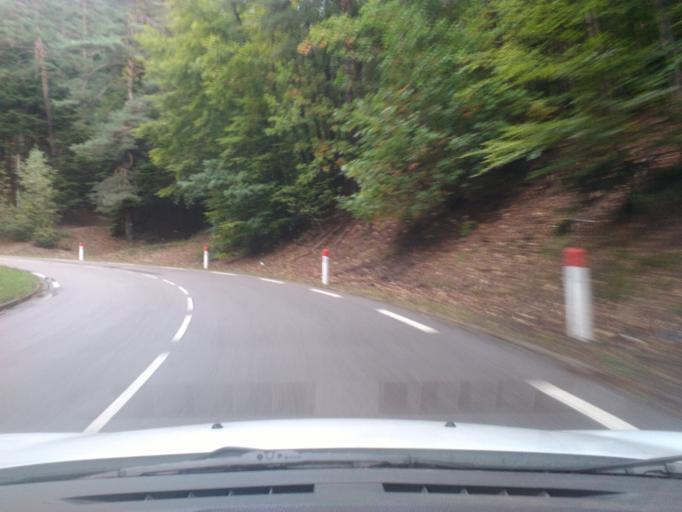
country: FR
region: Lorraine
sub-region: Departement des Vosges
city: Taintrux
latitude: 48.2776
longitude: 6.8785
